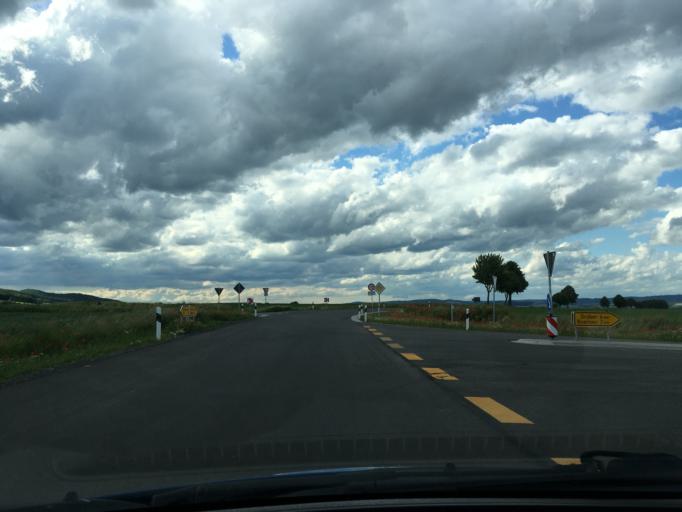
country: DE
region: Lower Saxony
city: Moringen
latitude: 51.7510
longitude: 9.8750
